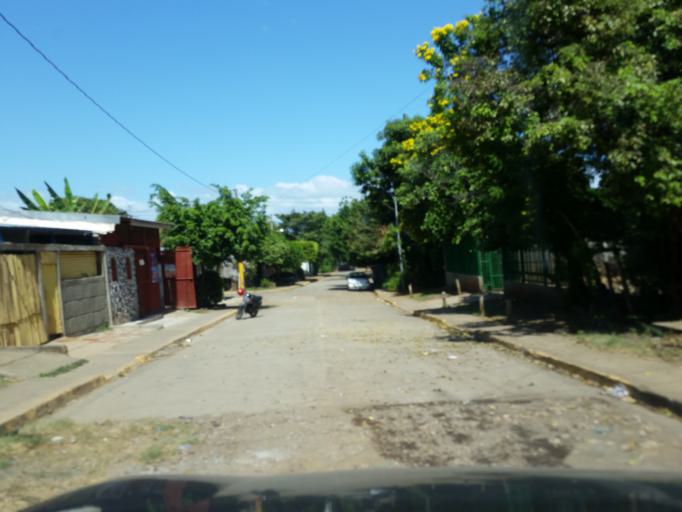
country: NI
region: Managua
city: Managua
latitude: 12.1193
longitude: -86.2254
